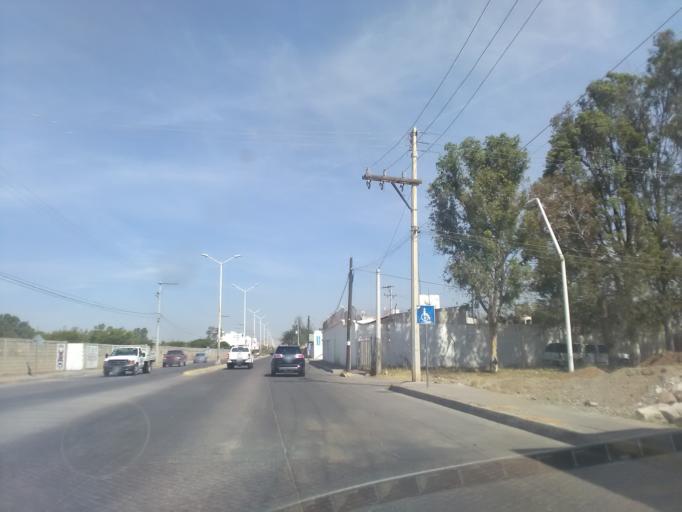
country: MX
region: Durango
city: Victoria de Durango
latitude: 24.0508
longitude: -104.6260
